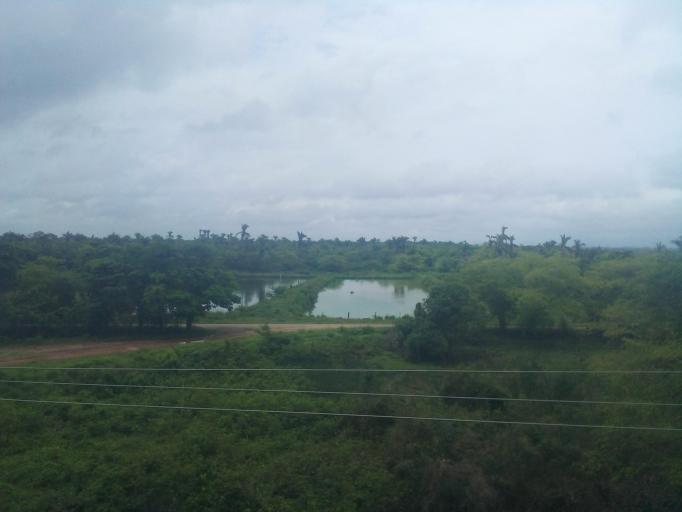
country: BR
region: Maranhao
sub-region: Vitoria Do Mearim
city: Vitoria do Mearim
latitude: -3.5438
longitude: -44.8367
